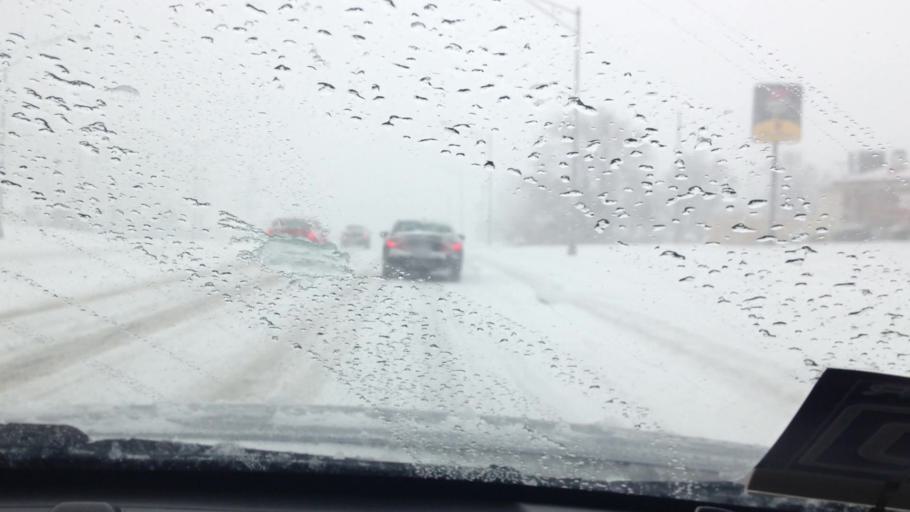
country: US
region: Kansas
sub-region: Wyandotte County
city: Kansas City
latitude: 39.1165
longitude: -94.6909
